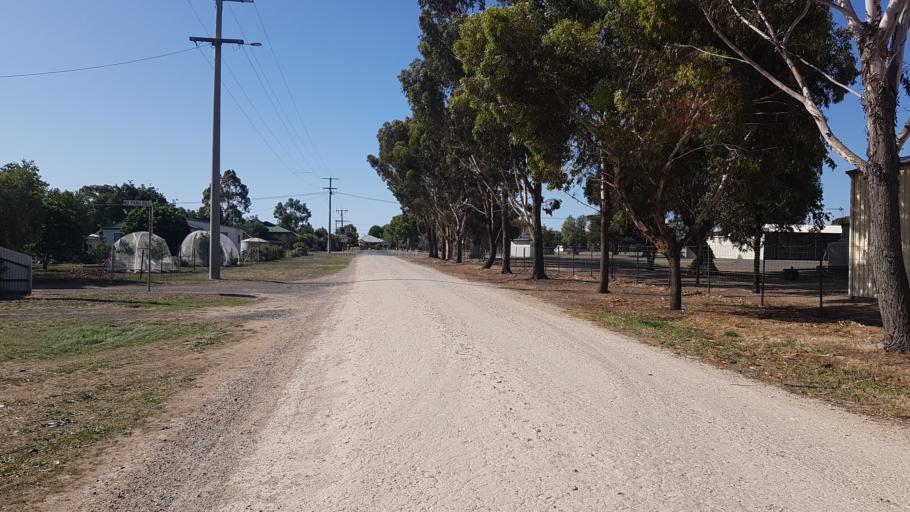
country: AU
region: Victoria
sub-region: Horsham
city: Horsham
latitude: -36.7429
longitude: 141.9473
